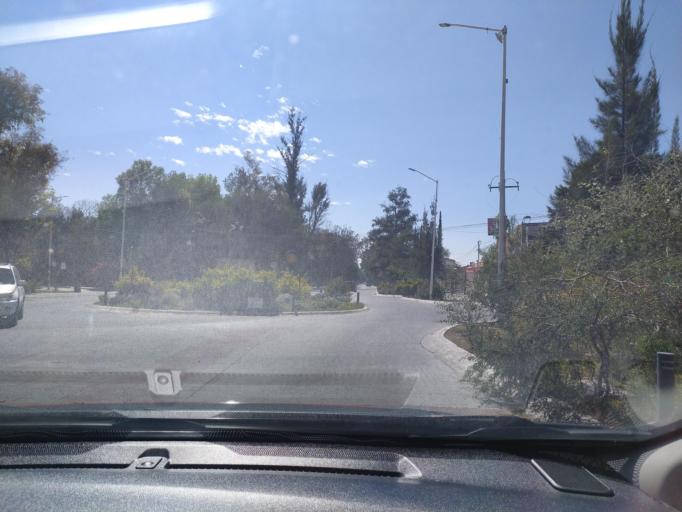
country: LA
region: Oudomxai
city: Muang La
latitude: 21.0312
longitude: 101.8302
